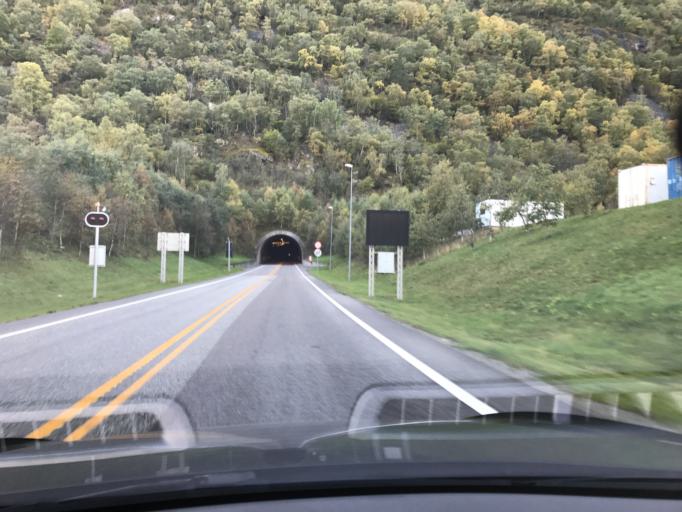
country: NO
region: Sogn og Fjordane
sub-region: Laerdal
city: Laerdalsoyri
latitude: 61.0644
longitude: 7.5042
